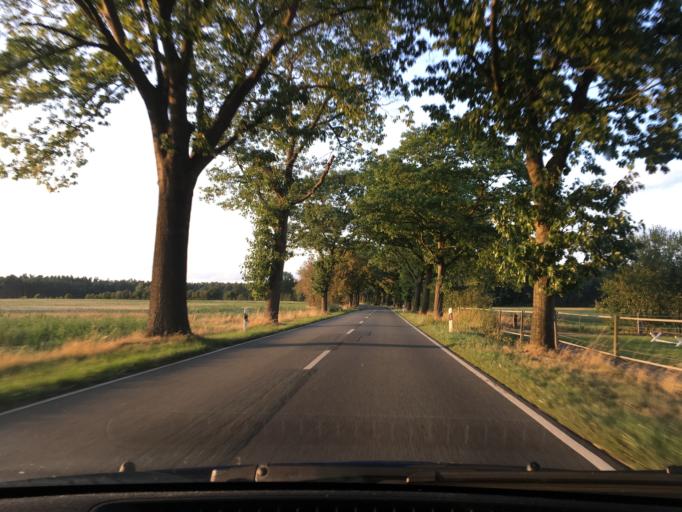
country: DE
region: Lower Saxony
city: Bleckede
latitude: 53.2638
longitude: 10.7435
